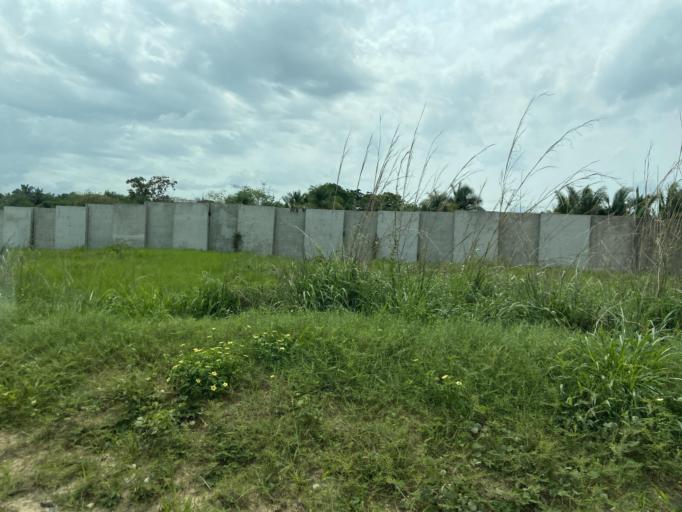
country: BR
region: Para
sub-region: Maraba
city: Maraba
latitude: -5.2959
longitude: -49.0660
